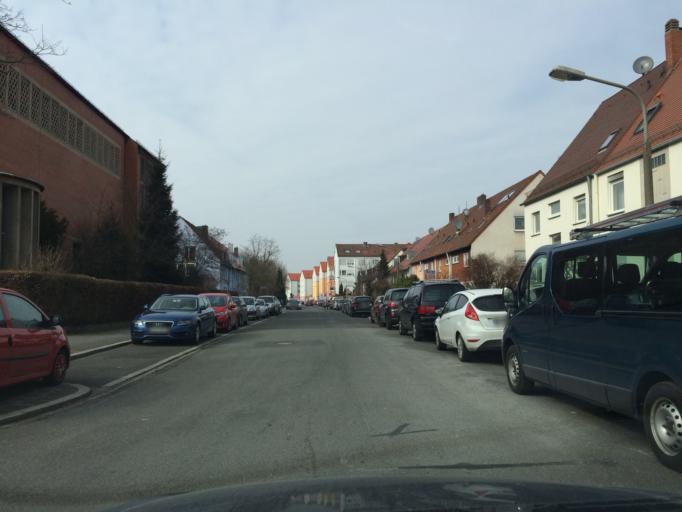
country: DE
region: Bavaria
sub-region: Regierungsbezirk Mittelfranken
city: Nuernberg
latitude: 49.4687
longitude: 11.1081
